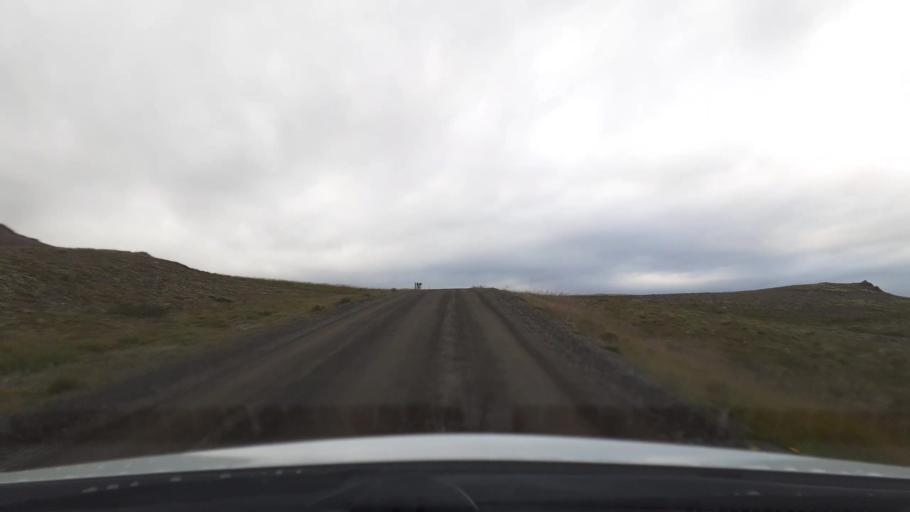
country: IS
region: Capital Region
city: Mosfellsbaer
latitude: 64.1996
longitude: -21.5581
